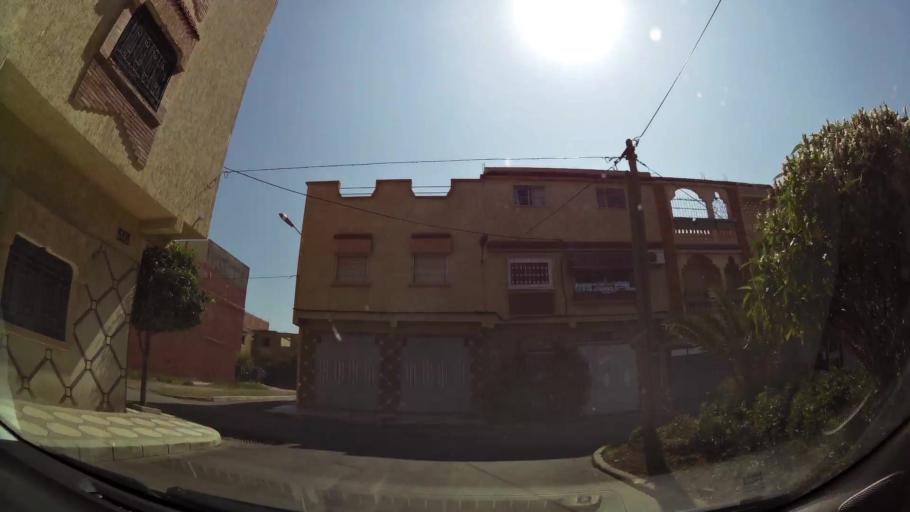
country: MA
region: Oriental
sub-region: Oujda-Angad
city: Oujda
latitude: 34.6938
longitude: -1.8767
